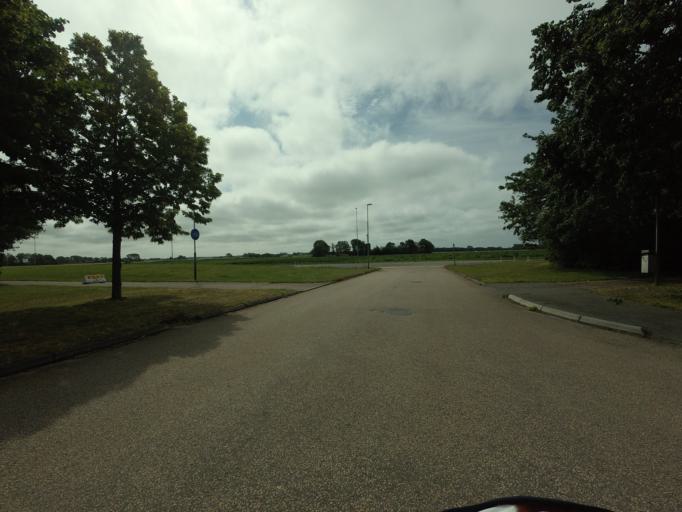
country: SE
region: Skane
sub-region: Hoganas Kommun
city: Hoganas
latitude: 56.1731
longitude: 12.5693
